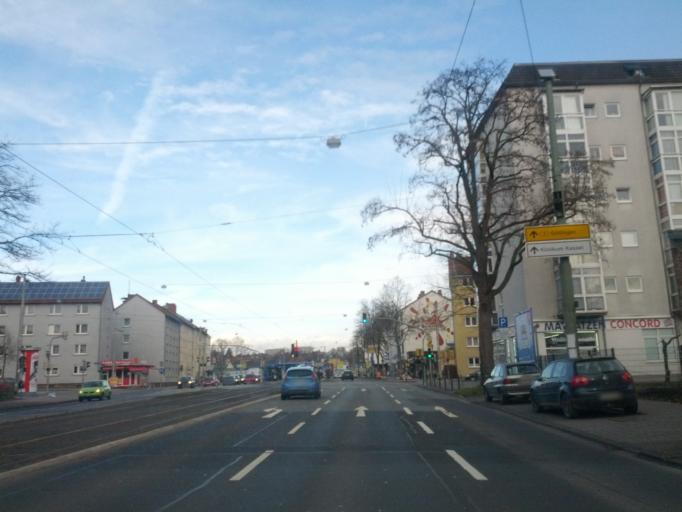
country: DE
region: Hesse
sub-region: Regierungsbezirk Kassel
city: Kassel
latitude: 51.3219
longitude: 9.5116
